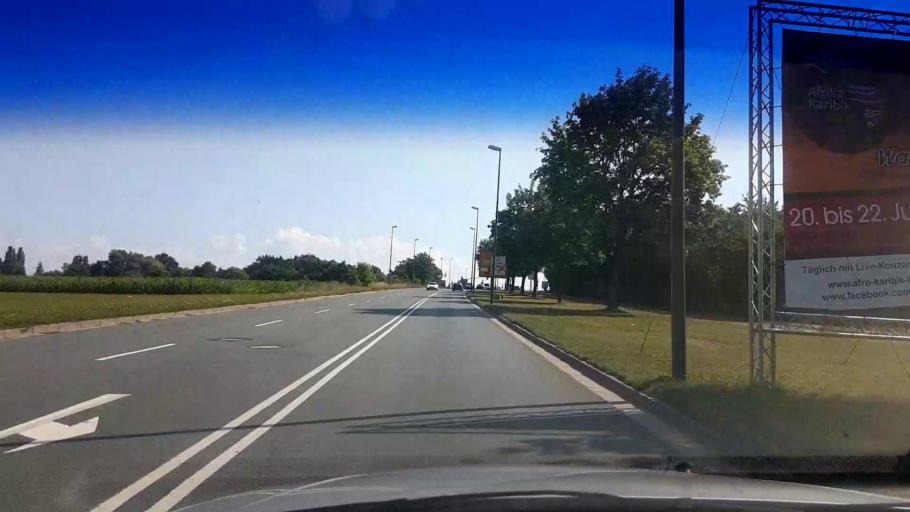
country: DE
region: Bavaria
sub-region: Upper Franconia
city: Bayreuth
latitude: 49.9266
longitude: 11.5943
